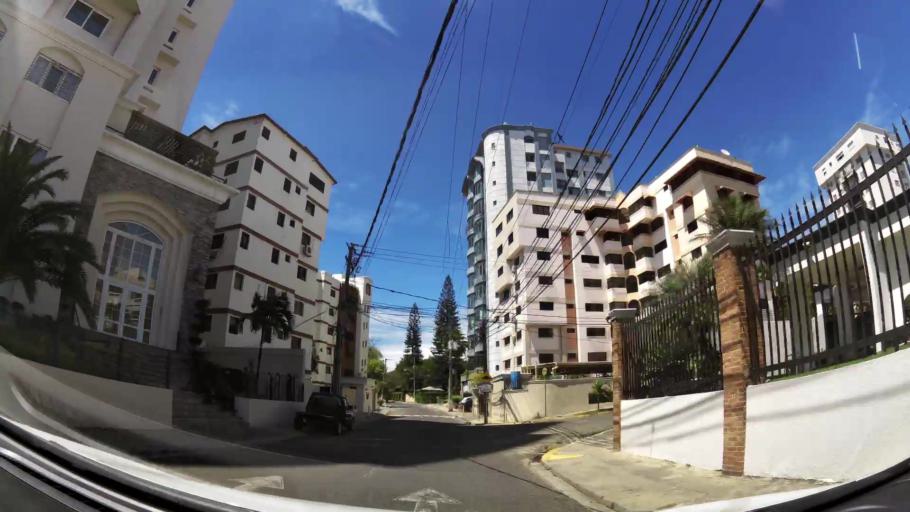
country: DO
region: Santiago
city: Santiago de los Caballeros
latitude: 19.4544
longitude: -70.6893
